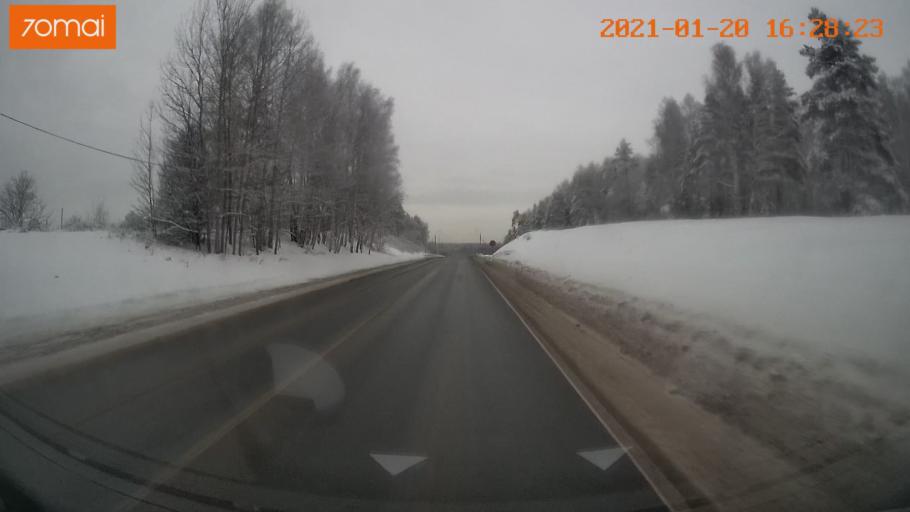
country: RU
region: Vladimir
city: Kameshkovo
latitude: 56.1949
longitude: 40.9184
